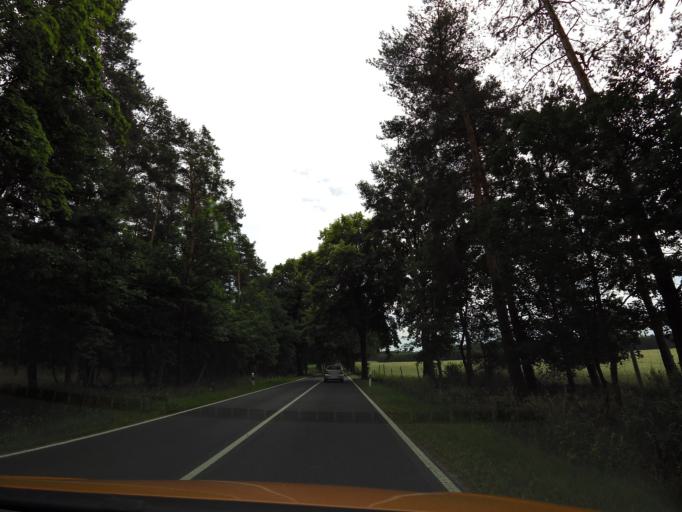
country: DE
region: Brandenburg
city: Am Mellensee
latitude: 52.2359
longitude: 13.3935
